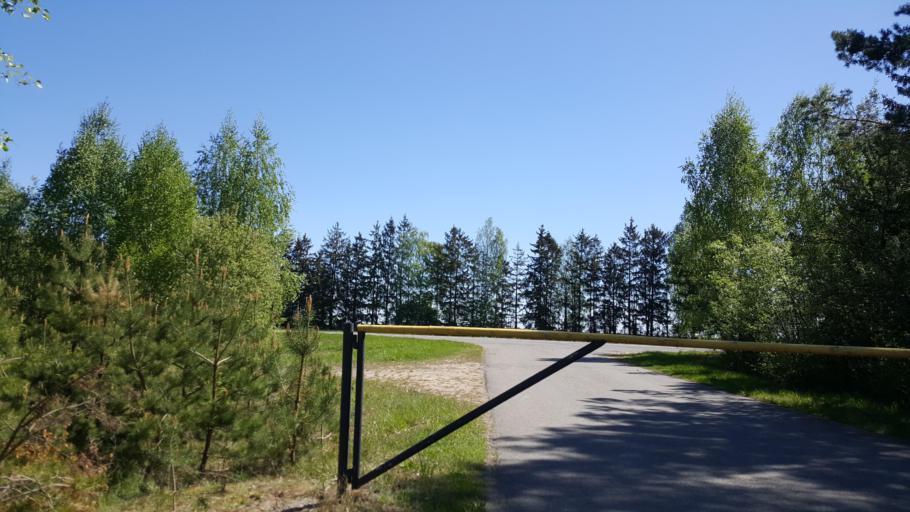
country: BY
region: Brest
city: Kamyanyets
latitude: 52.4504
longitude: 23.7826
